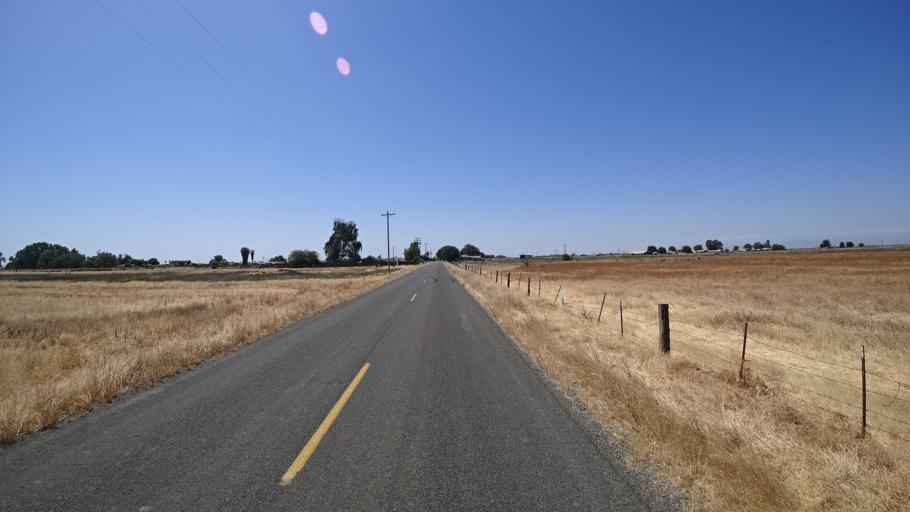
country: US
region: California
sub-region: Kings County
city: Lemoore
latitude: 36.2732
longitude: -119.7900
